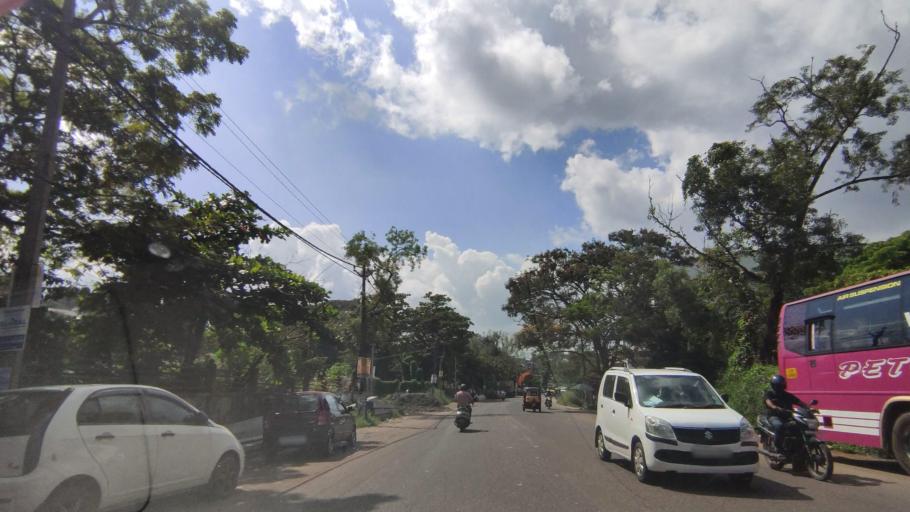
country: IN
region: Kerala
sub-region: Kottayam
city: Kottayam
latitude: 9.5939
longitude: 76.5275
